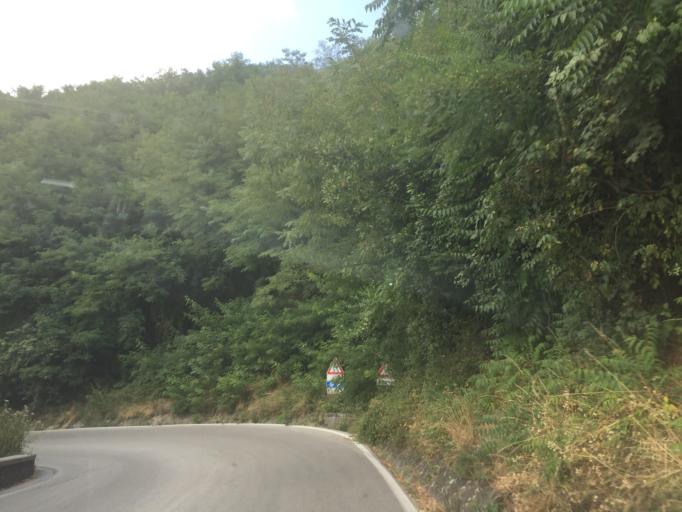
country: IT
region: Tuscany
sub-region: Provincia di Pistoia
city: San Marcello Pistoiese
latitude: 44.0579
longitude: 10.7705
